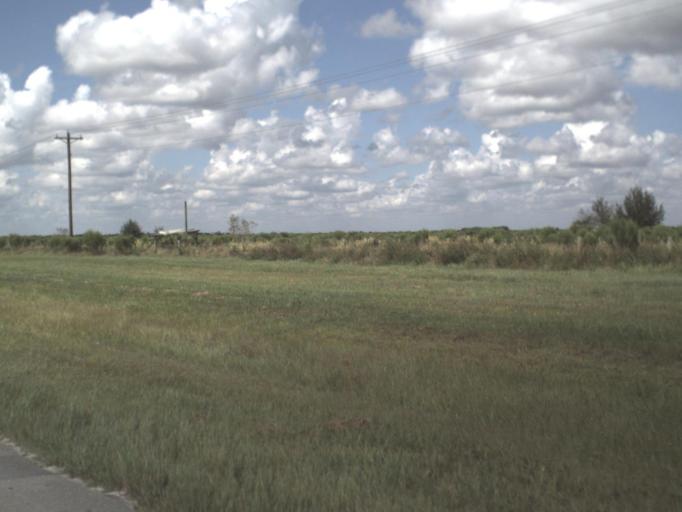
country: US
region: Florida
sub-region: Collier County
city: Immokalee
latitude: 26.4902
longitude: -81.4525
